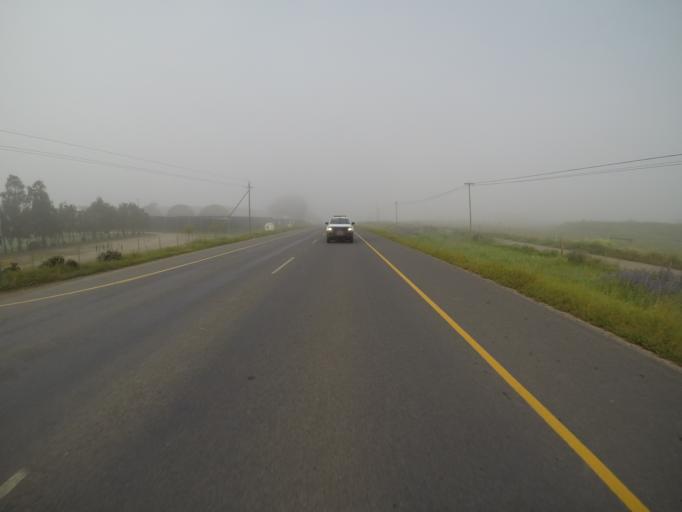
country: ZA
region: Western Cape
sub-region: City of Cape Town
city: Kraaifontein
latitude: -33.7716
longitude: 18.7105
